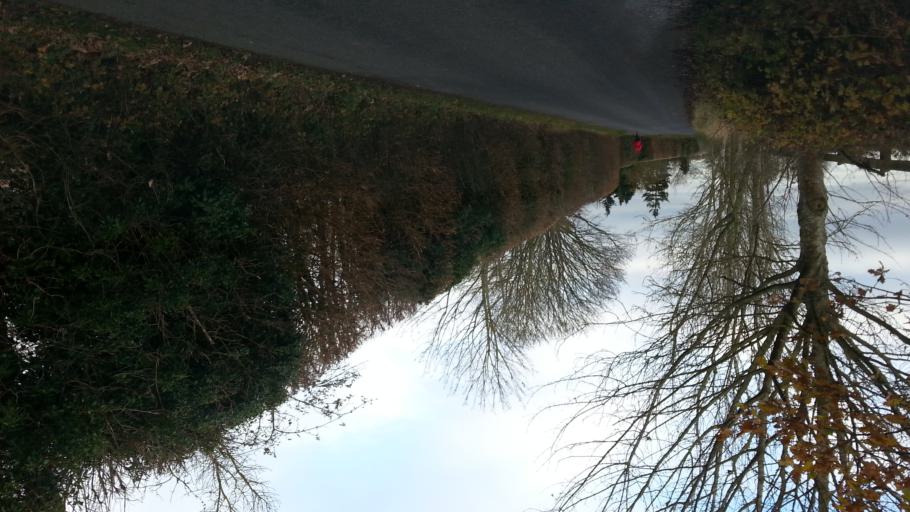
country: GB
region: England
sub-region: Suffolk
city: Ixworth
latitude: 52.3261
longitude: 0.8774
